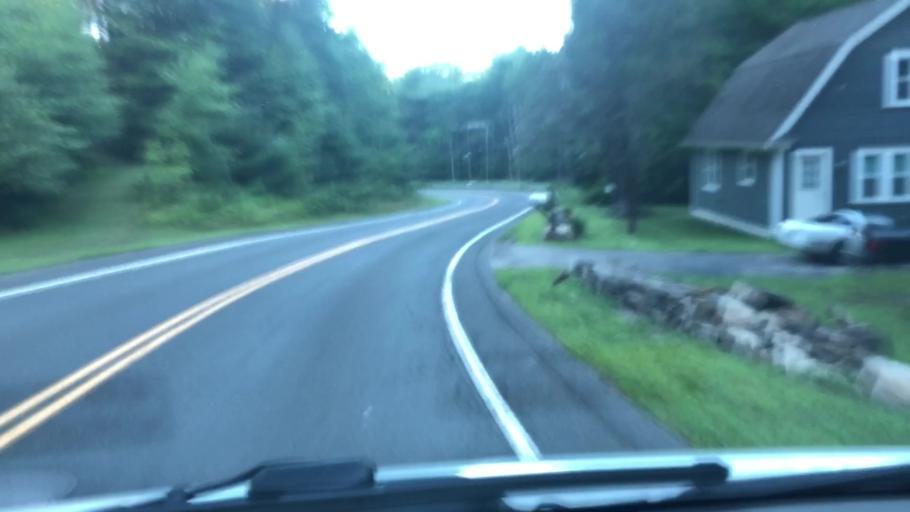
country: US
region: Massachusetts
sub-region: Hampshire County
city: Westhampton
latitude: 42.2824
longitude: -72.8601
